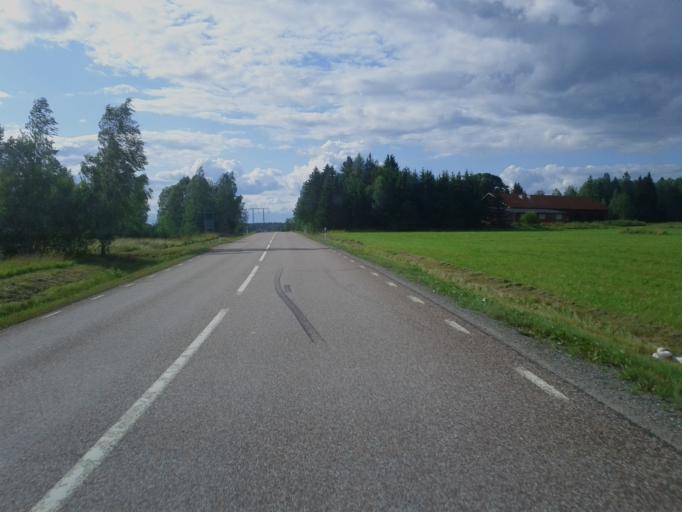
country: SE
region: Vaestmanland
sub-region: Sala Kommun
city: Sala
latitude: 59.9150
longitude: 16.5173
